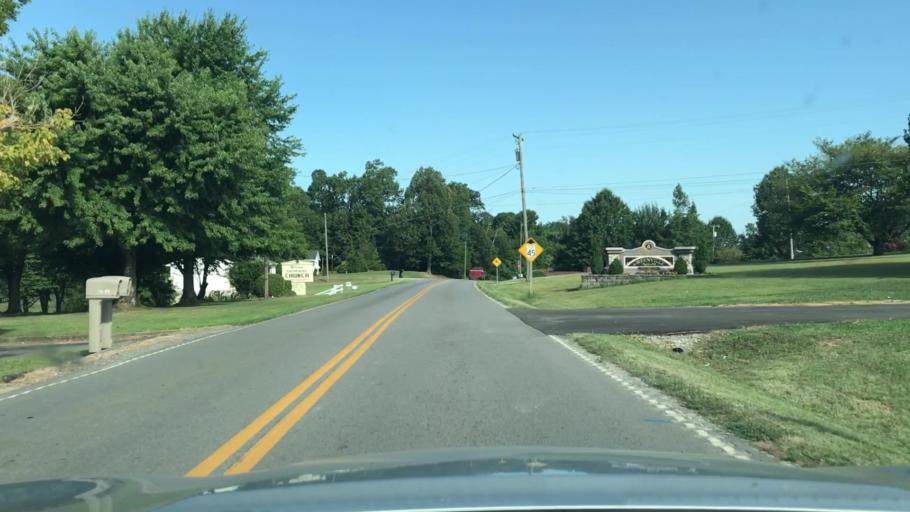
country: US
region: Kentucky
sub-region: Muhlenberg County
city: Greenville
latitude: 37.1889
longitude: -87.1694
